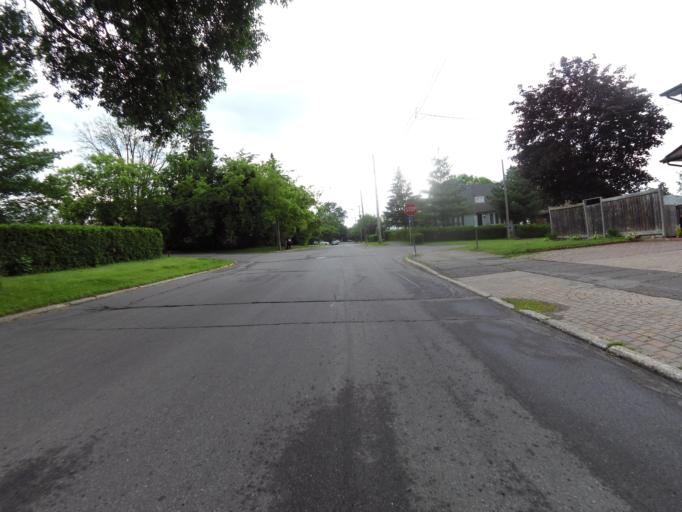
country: CA
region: Ontario
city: Ottawa
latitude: 45.3764
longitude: -75.7305
